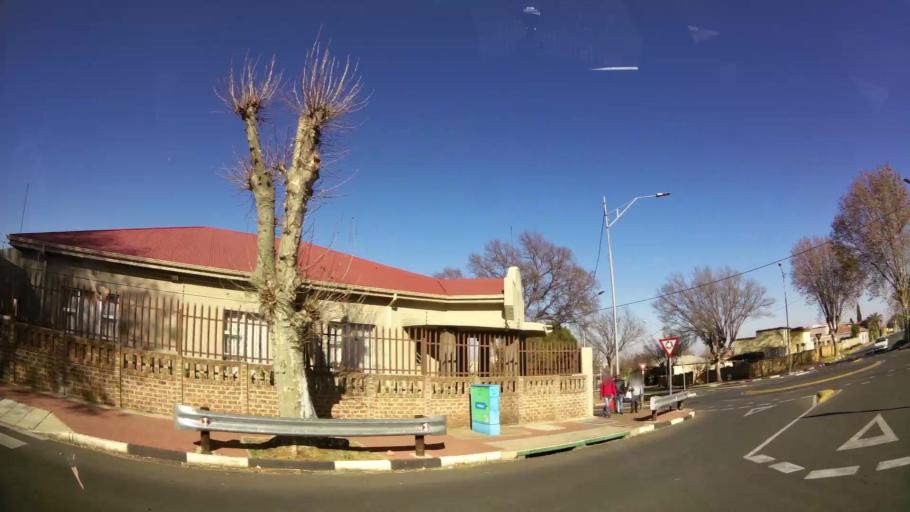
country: ZA
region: Gauteng
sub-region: City of Johannesburg Metropolitan Municipality
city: Johannesburg
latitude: -26.1969
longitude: 27.9939
